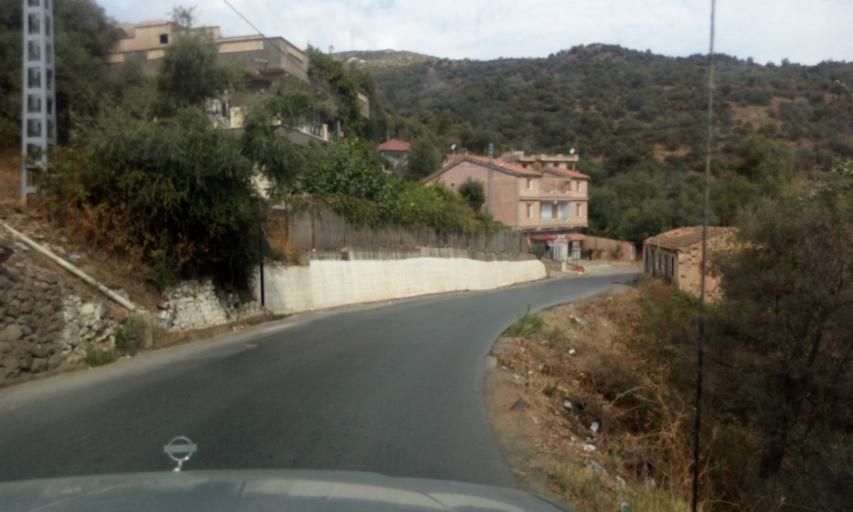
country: DZ
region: Tizi Ouzou
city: Chemini
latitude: 36.6184
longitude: 4.6633
